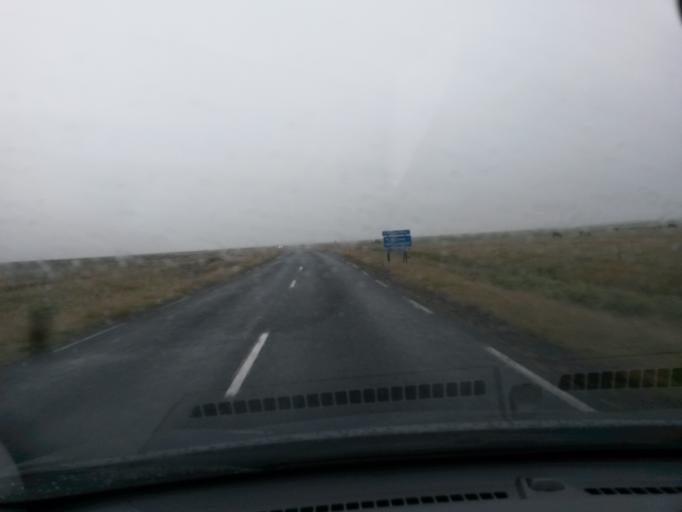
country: IS
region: South
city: Vestmannaeyjar
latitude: 63.5379
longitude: -19.6466
